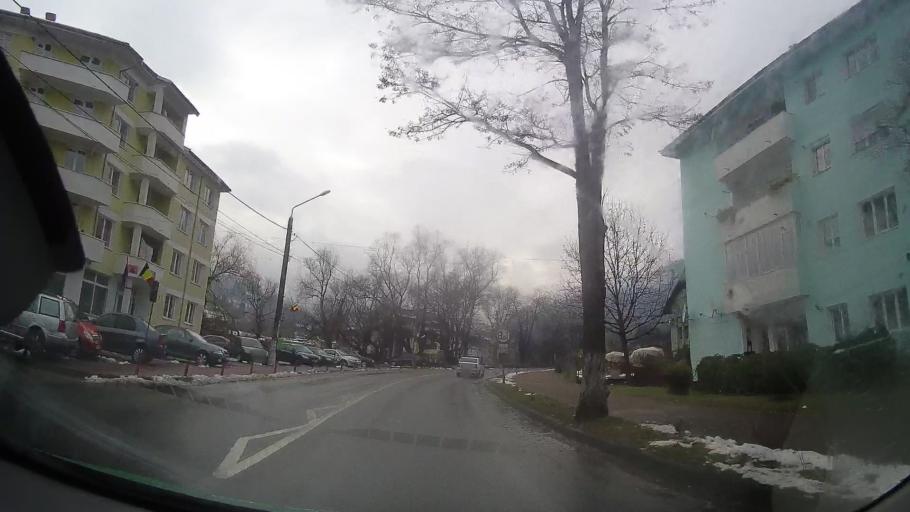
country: RO
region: Neamt
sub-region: Comuna Bicaz
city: Dodeni
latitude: 46.9109
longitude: 26.0872
